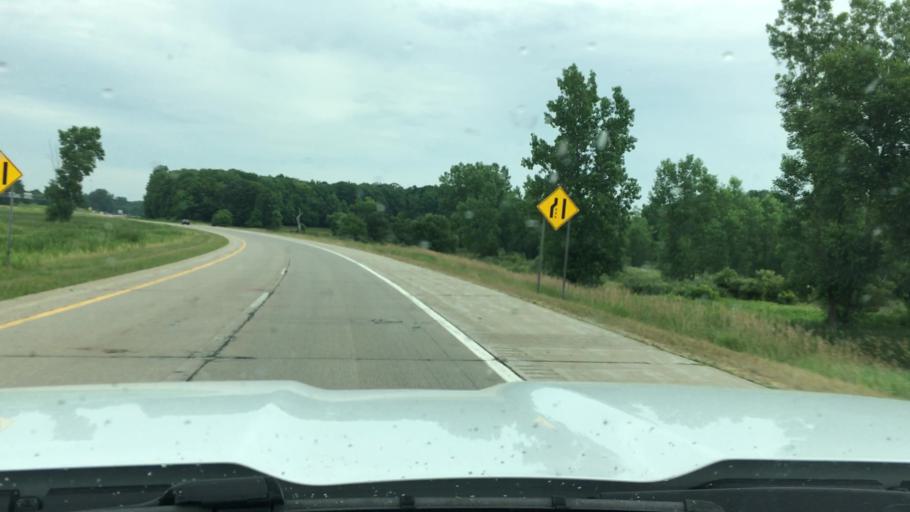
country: US
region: Michigan
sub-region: Clinton County
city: Wacousta
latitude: 42.7887
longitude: -84.6571
